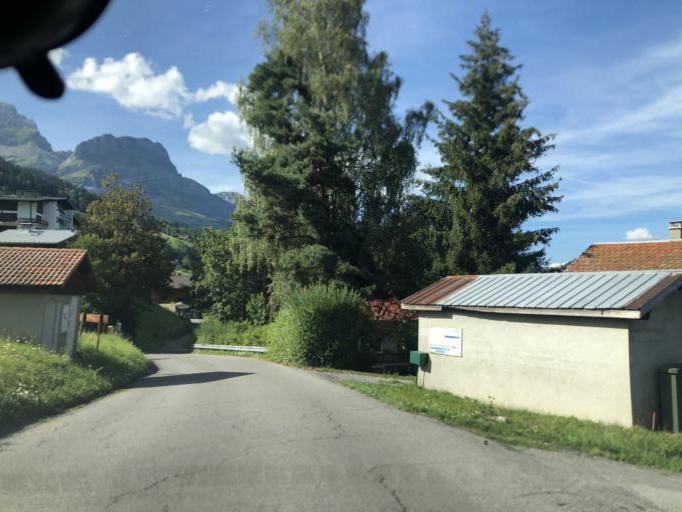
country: FR
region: Rhone-Alpes
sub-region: Departement de la Haute-Savoie
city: Cordon
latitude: 45.9138
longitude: 6.6021
